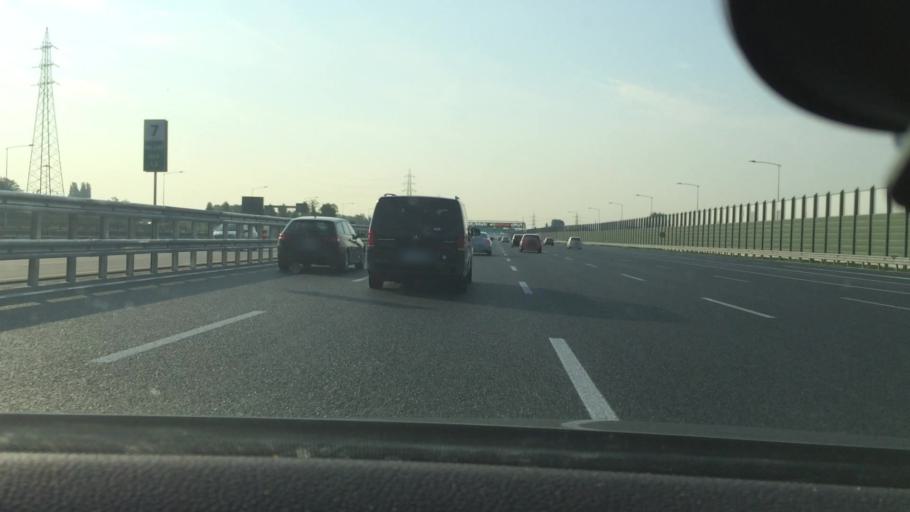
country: IT
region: Lombardy
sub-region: Citta metropolitana di Milano
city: Passirana
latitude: 45.5561
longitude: 9.0448
